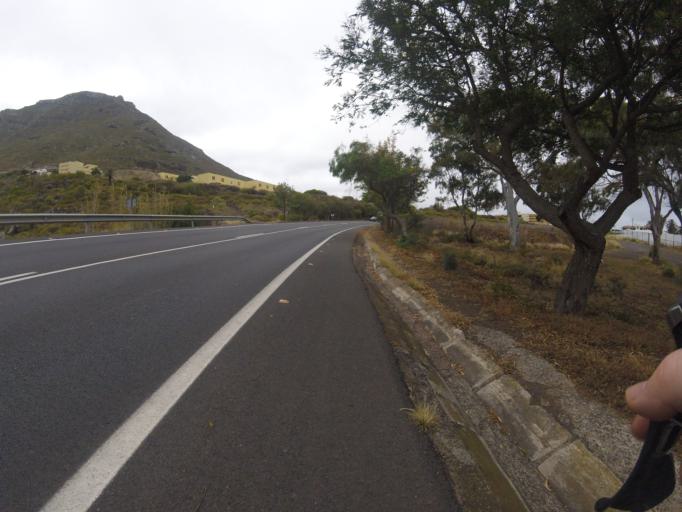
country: ES
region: Canary Islands
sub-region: Provincia de Santa Cruz de Tenerife
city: Tegueste
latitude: 28.5461
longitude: -16.3494
